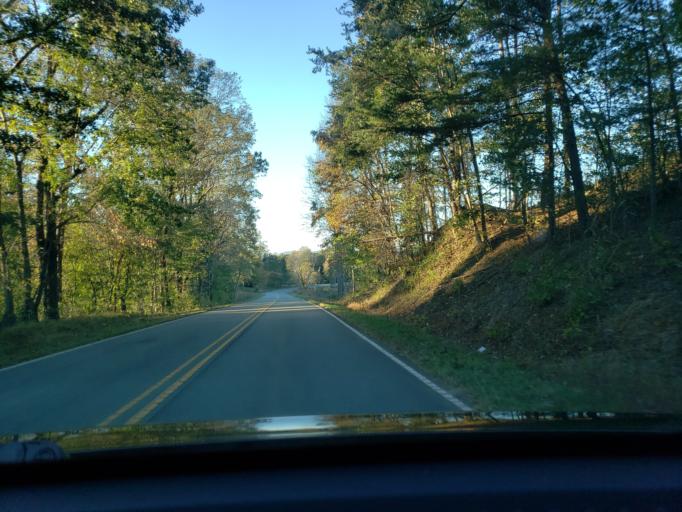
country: US
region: North Carolina
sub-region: Forsyth County
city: Walkertown
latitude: 36.2300
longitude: -80.1994
